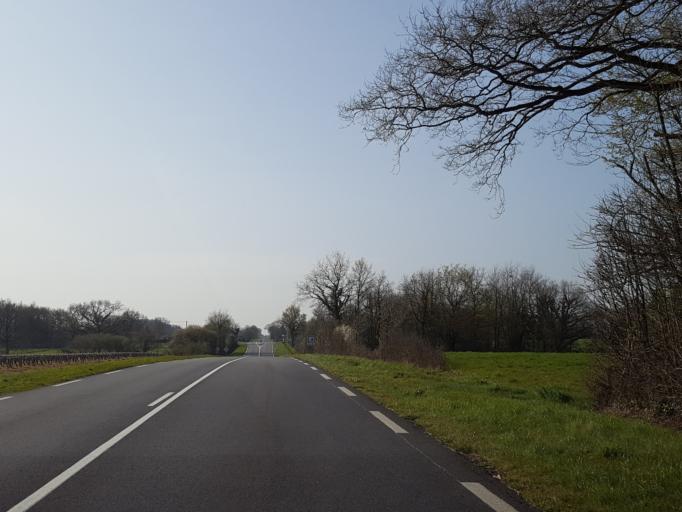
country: FR
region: Pays de la Loire
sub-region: Departement de la Vendee
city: Rocheserviere
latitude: 46.8947
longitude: -1.5021
